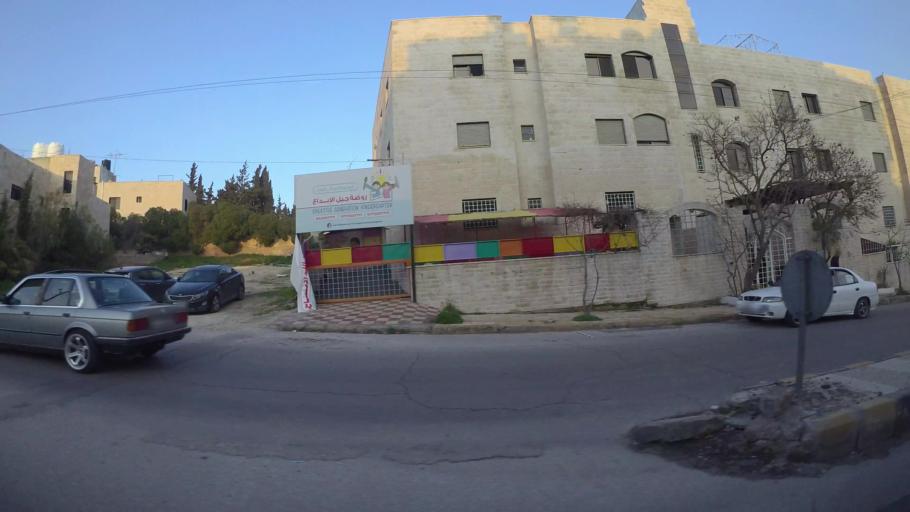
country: JO
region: Amman
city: Amman
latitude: 31.9949
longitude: 35.9531
